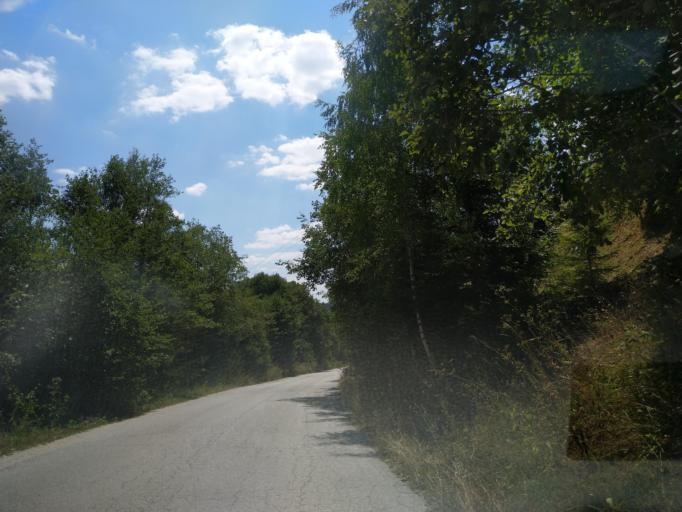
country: RS
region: Central Serbia
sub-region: Zlatiborski Okrug
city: Nova Varos
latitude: 43.4604
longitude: 19.9756
